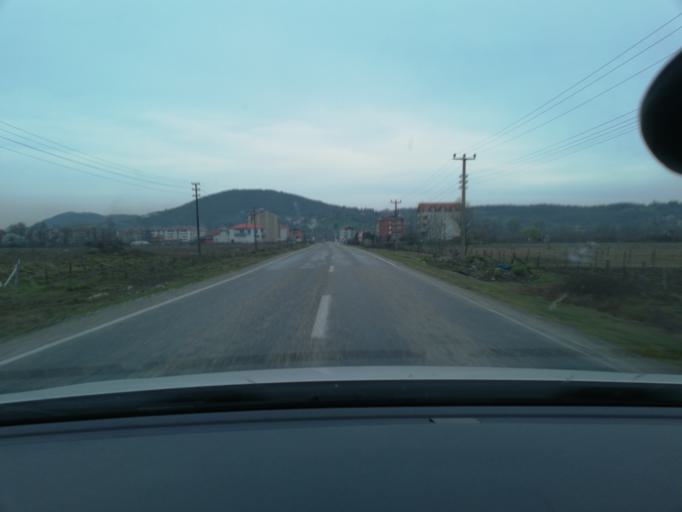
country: TR
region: Zonguldak
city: Saltukova
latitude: 41.5210
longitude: 32.1018
